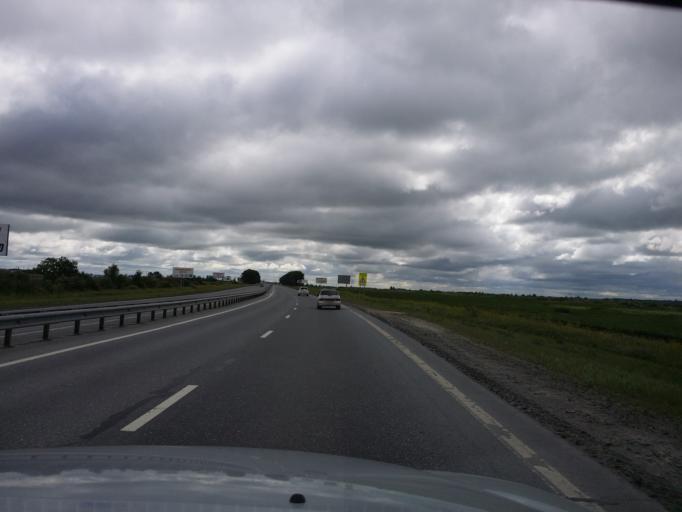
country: RU
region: Tjumen
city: Antipino
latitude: 57.1591
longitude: 65.8192
